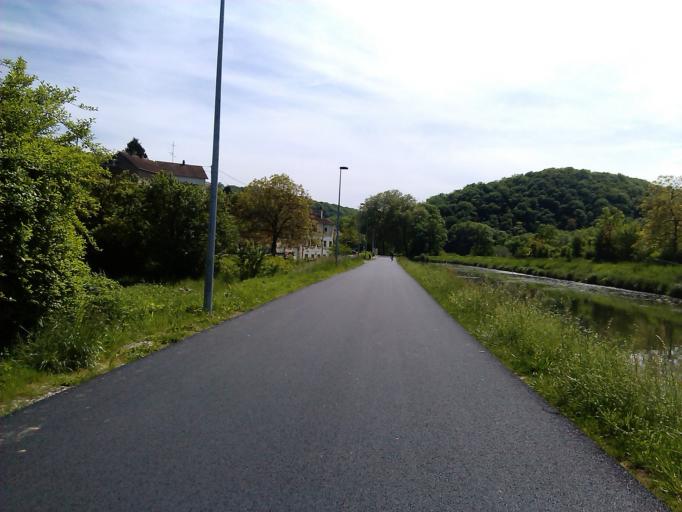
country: FR
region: Franche-Comte
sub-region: Departement du Doubs
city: Avanne-Aveney
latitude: 47.1968
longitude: 5.9593
